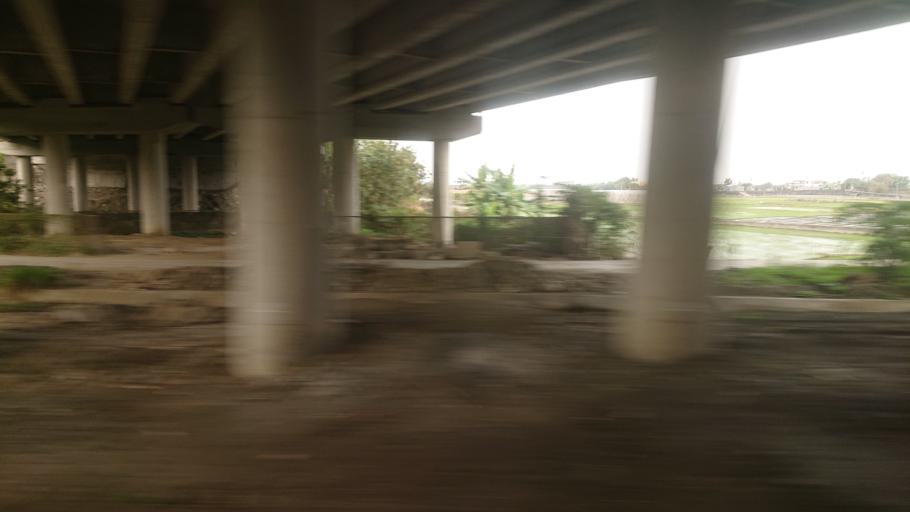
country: TW
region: Taiwan
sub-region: Yunlin
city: Douliu
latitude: 23.7739
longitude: 120.6372
